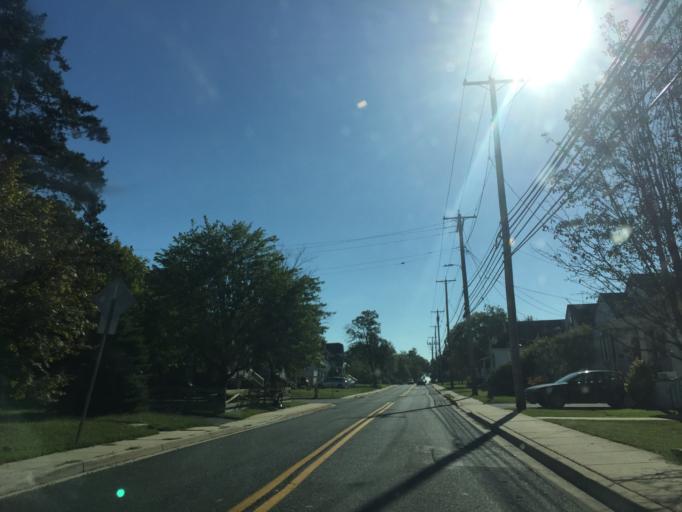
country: US
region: Maryland
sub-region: Baltimore County
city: Overlea
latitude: 39.3563
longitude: -76.5171
